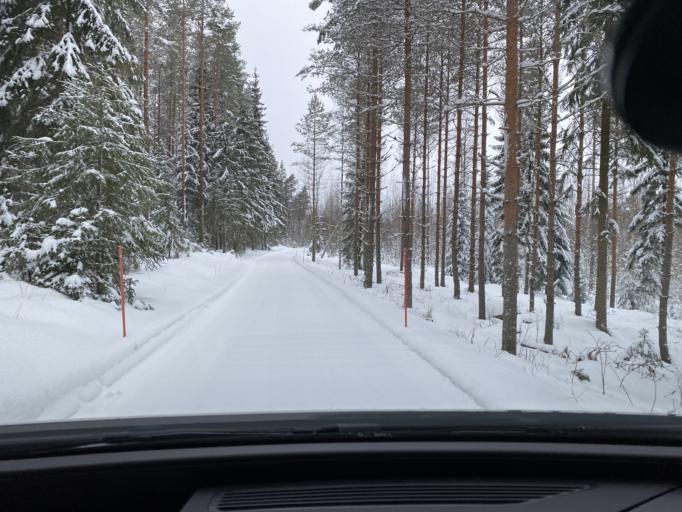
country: FI
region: Pirkanmaa
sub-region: Lounais-Pirkanmaa
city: Punkalaidun
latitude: 61.1343
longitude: 23.0957
